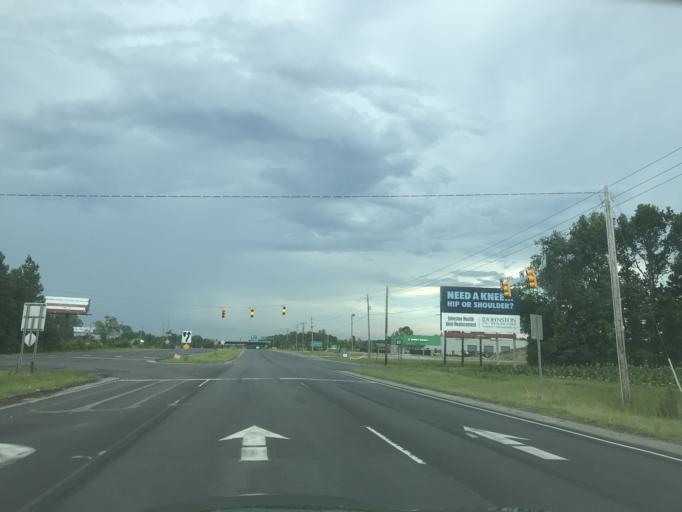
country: US
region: North Carolina
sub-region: Johnston County
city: Clayton
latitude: 35.6091
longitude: -78.4168
